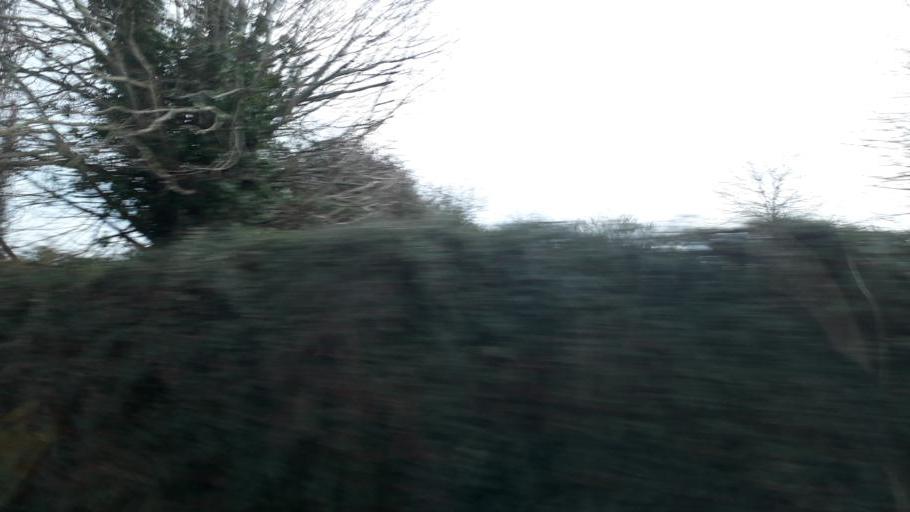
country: IE
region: Leinster
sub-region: Fingal County
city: Skerries
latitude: 53.5694
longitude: -6.1219
